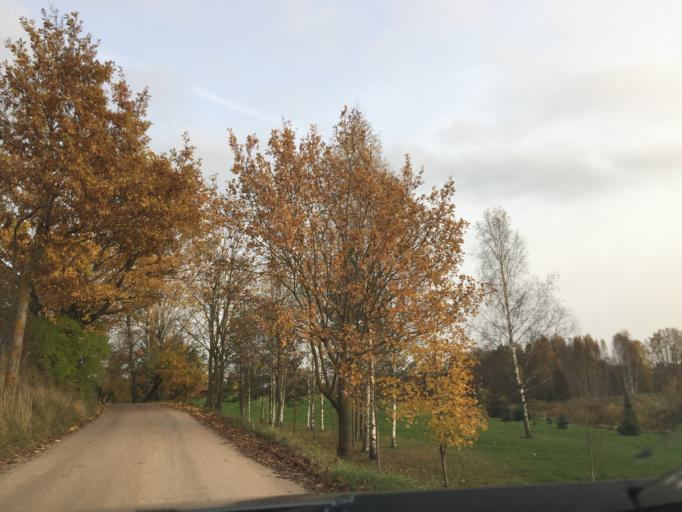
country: LV
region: Pargaujas
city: Stalbe
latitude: 57.3217
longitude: 25.1417
